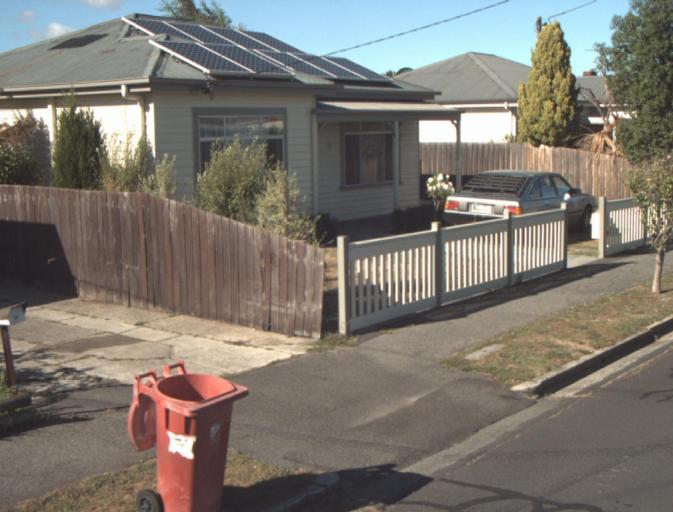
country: AU
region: Tasmania
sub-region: Launceston
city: Newnham
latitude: -41.4015
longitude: 147.1364
